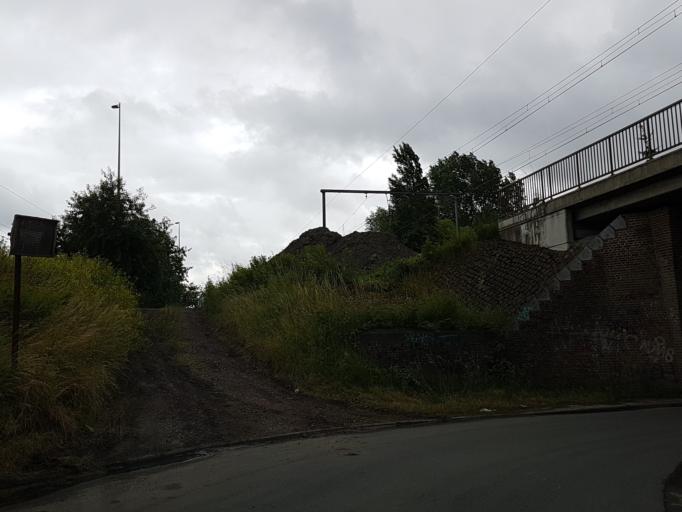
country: BE
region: Flanders
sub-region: Provincie Oost-Vlaanderen
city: Aalst
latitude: 50.9496
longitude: 4.0257
